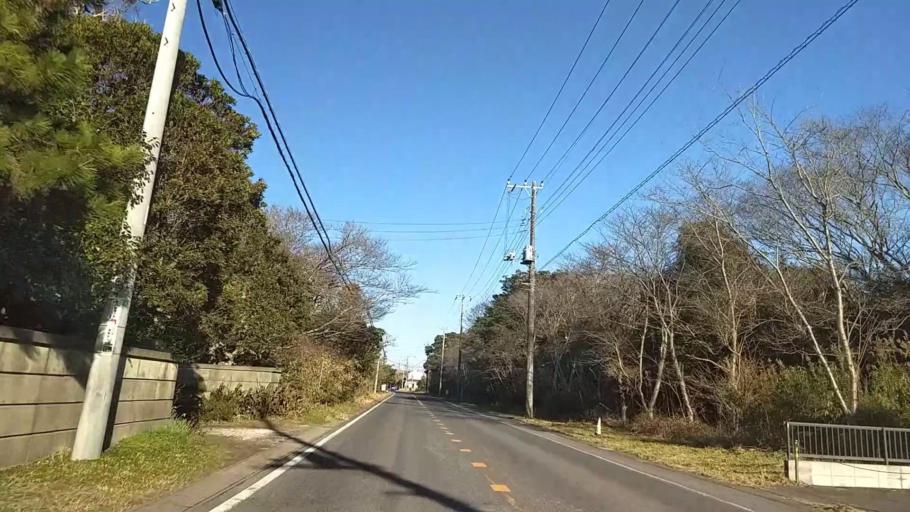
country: JP
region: Chiba
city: Yokaichiba
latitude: 35.6106
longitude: 140.5236
